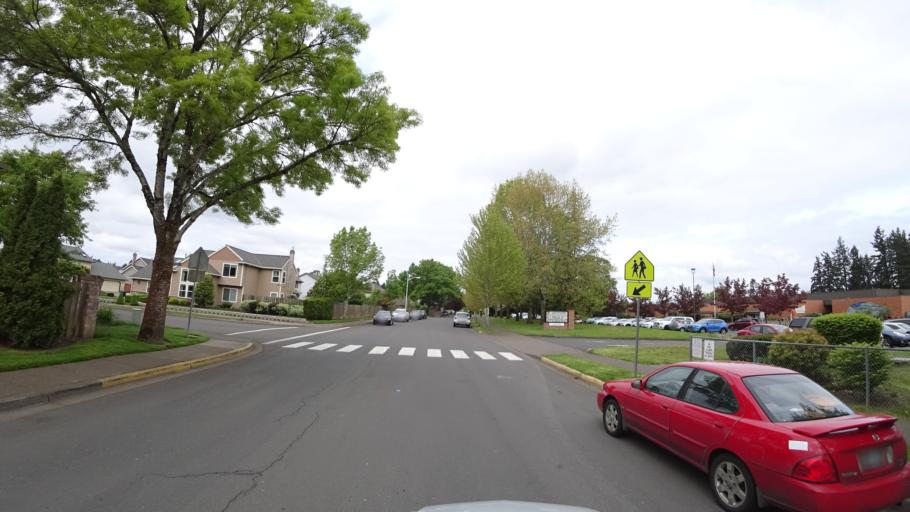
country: US
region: Oregon
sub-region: Washington County
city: Hillsboro
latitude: 45.5429
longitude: -122.9806
